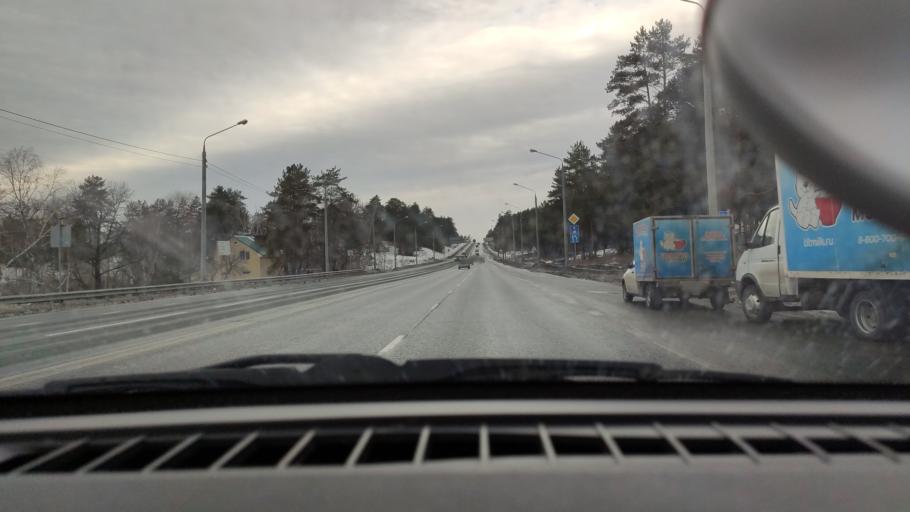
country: RU
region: Samara
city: Volzhskiy
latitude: 53.4386
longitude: 50.1097
